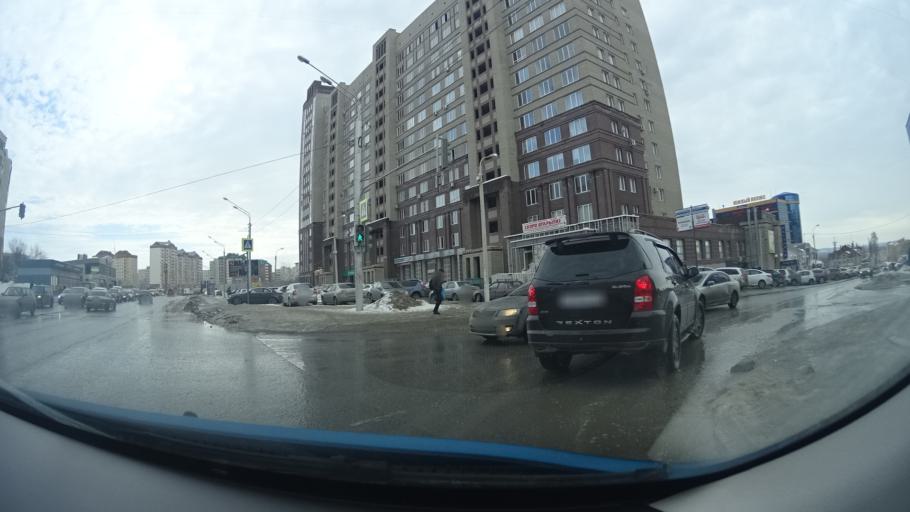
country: RU
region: Bashkortostan
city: Ufa
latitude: 54.6981
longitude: 55.9907
